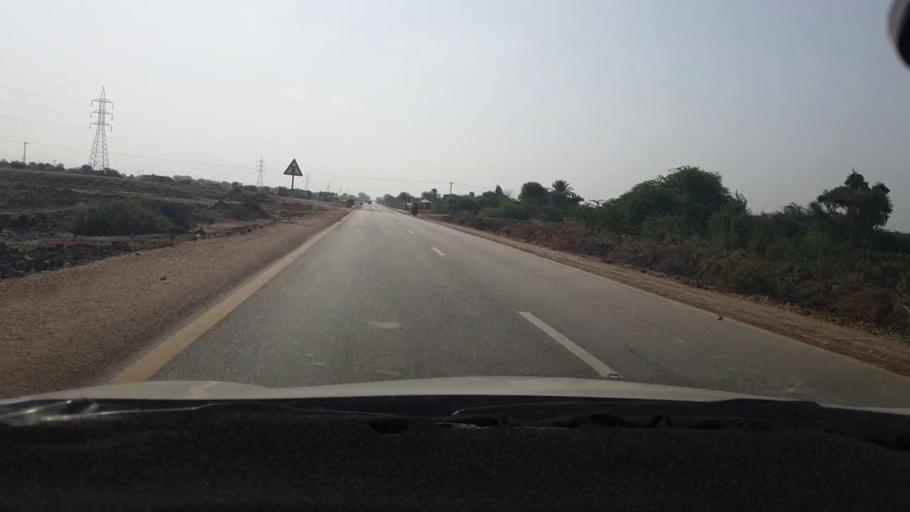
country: PK
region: Sindh
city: Jhol
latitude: 25.9125
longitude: 69.0118
